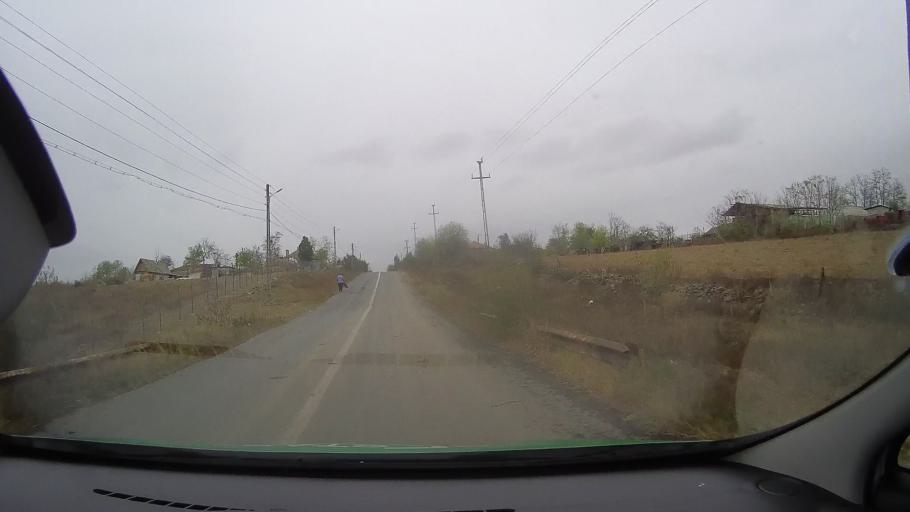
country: RO
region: Constanta
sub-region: Comuna Pantelimon
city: Pantelimon
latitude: 44.5428
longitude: 28.3291
